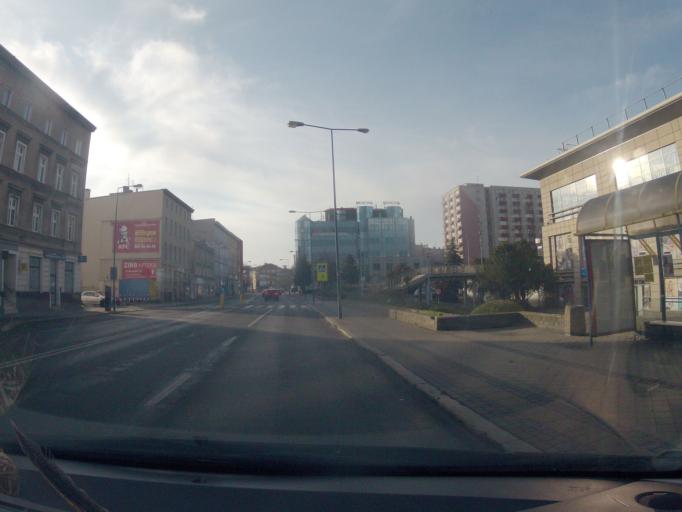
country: PL
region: Opole Voivodeship
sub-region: Powiat opolski
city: Opole
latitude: 50.6678
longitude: 17.9311
